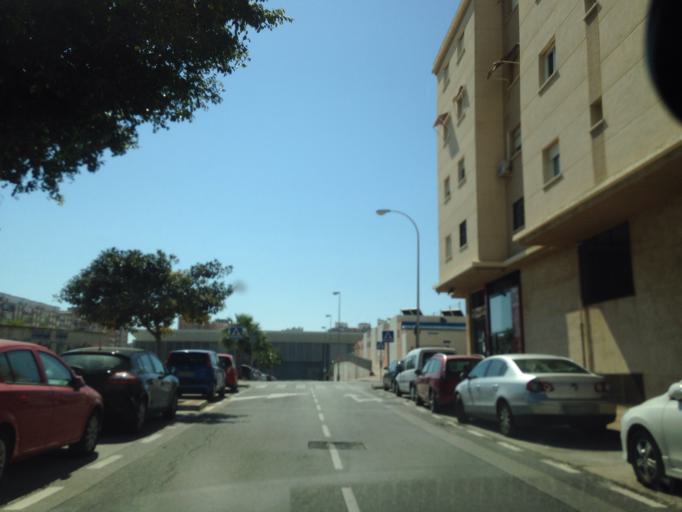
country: ES
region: Andalusia
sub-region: Provincia de Malaga
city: Malaga
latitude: 36.7025
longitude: -4.4553
